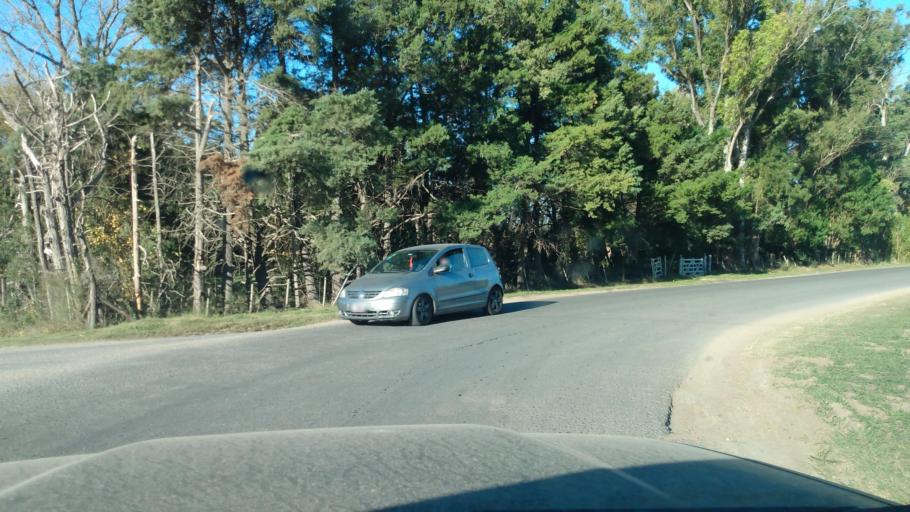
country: AR
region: Buenos Aires
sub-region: Partido de Lujan
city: Lujan
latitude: -34.4844
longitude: -59.2161
